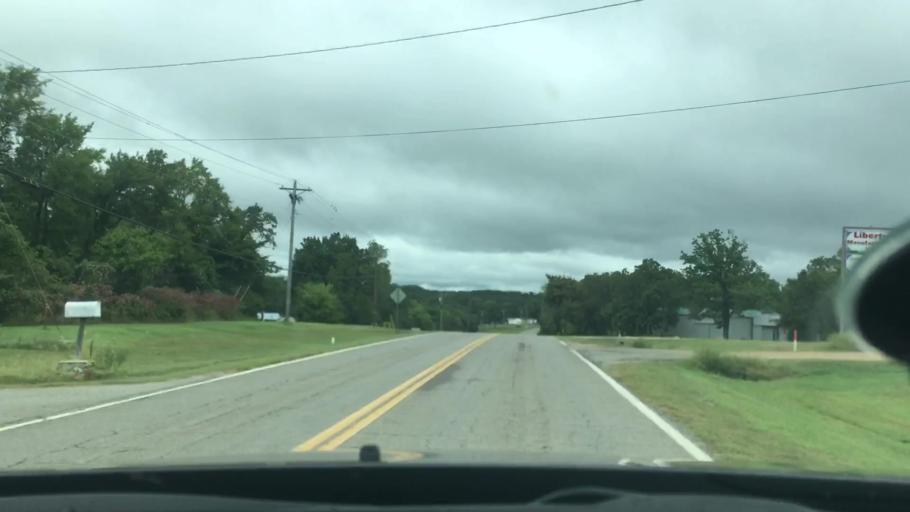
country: US
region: Oklahoma
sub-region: Cherokee County
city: Park Hill
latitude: 35.6905
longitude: -94.9118
